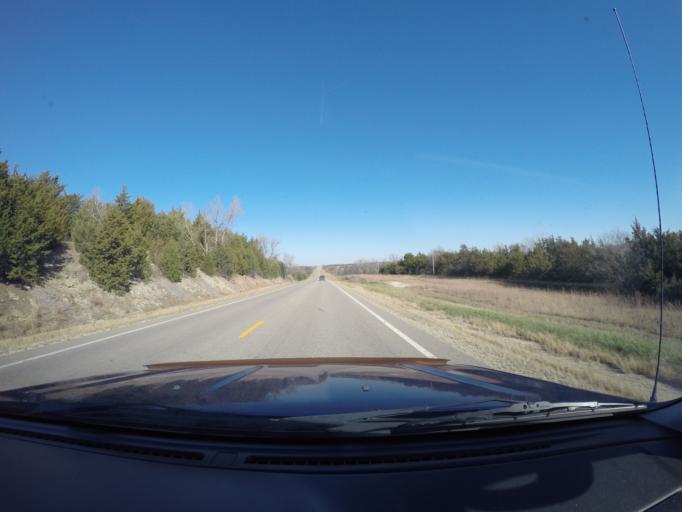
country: US
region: Kansas
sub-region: Riley County
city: Ogden
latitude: 39.3179
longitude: -96.7557
